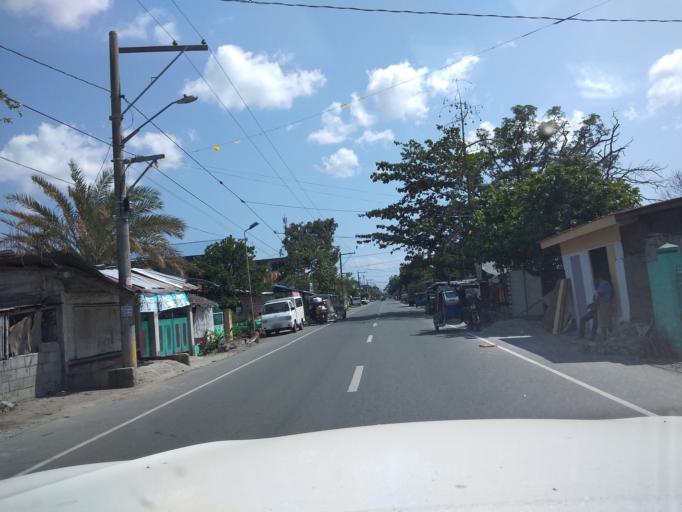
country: PH
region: Central Luzon
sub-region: Province of Pampanga
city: Bahay Pare
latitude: 15.0374
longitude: 120.8803
